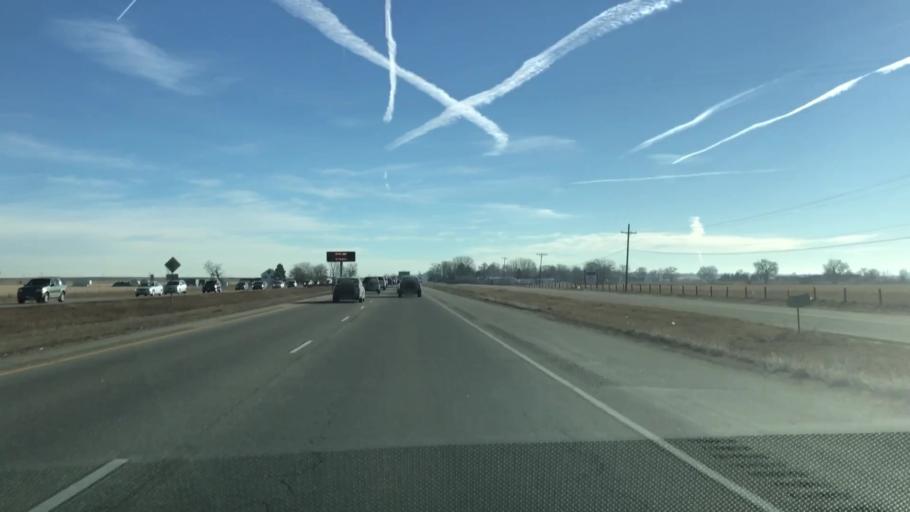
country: US
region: Colorado
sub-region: Weld County
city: Johnstown
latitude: 40.4073
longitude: -104.9618
